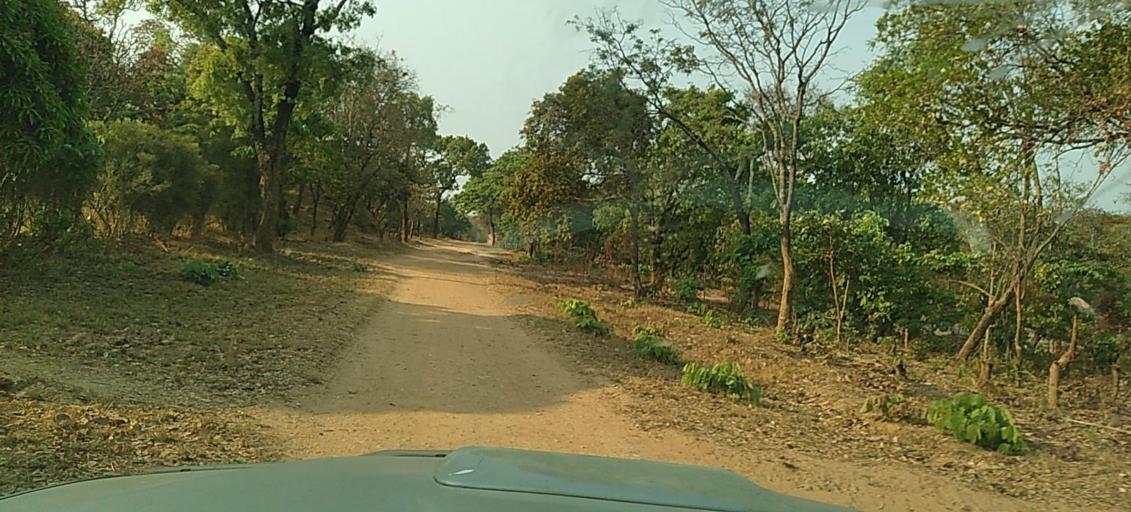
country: ZM
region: North-Western
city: Kasempa
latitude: -13.2779
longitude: 26.5555
